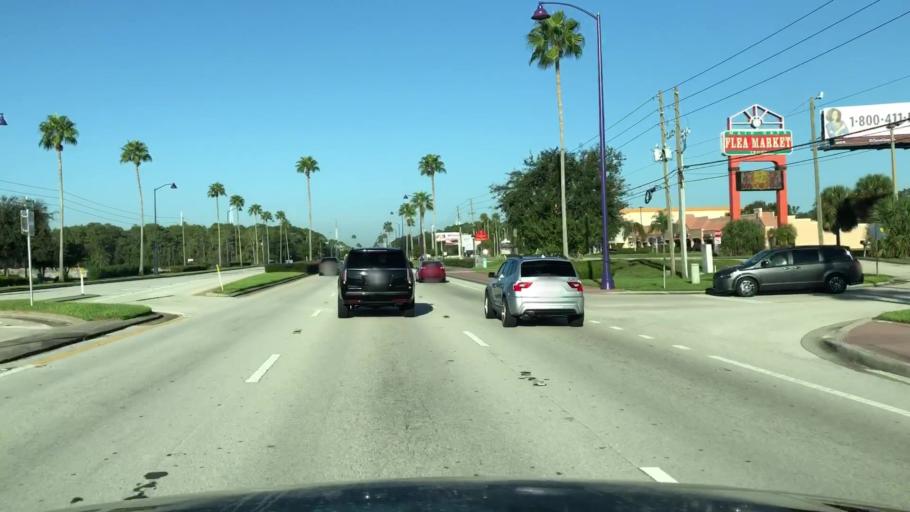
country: US
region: Florida
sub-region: Osceola County
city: Celebration
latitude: 28.3330
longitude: -81.4995
